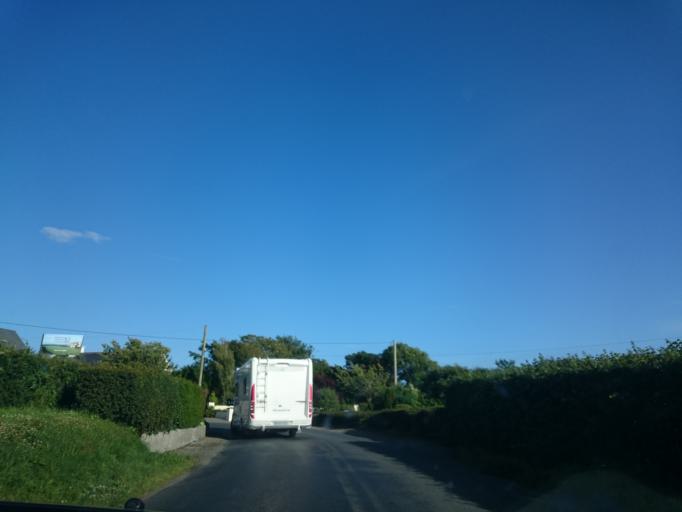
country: IE
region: Leinster
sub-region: Loch Garman
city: Loch Garman
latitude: 52.1849
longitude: -6.5724
